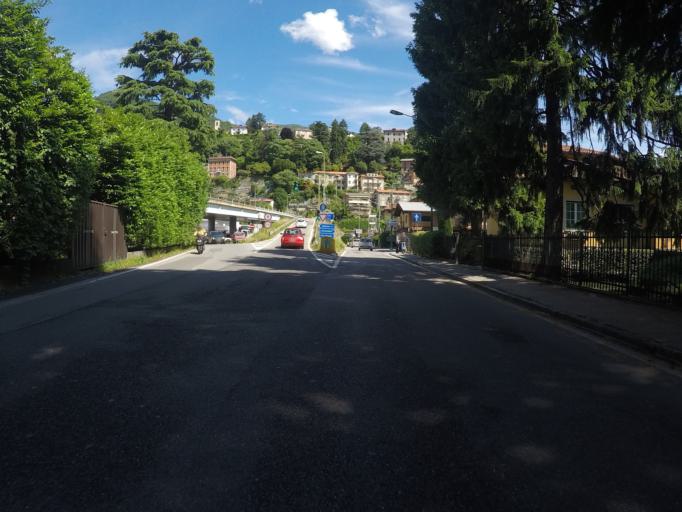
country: IT
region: Lombardy
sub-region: Provincia di Como
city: Cernobbio
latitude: 45.8370
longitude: 9.0677
